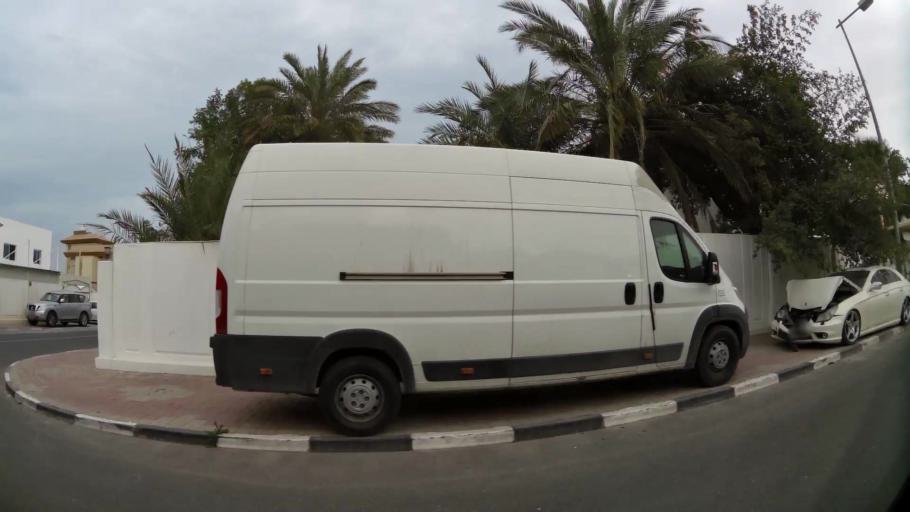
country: QA
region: Baladiyat ad Dawhah
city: Doha
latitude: 25.3278
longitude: 51.5074
